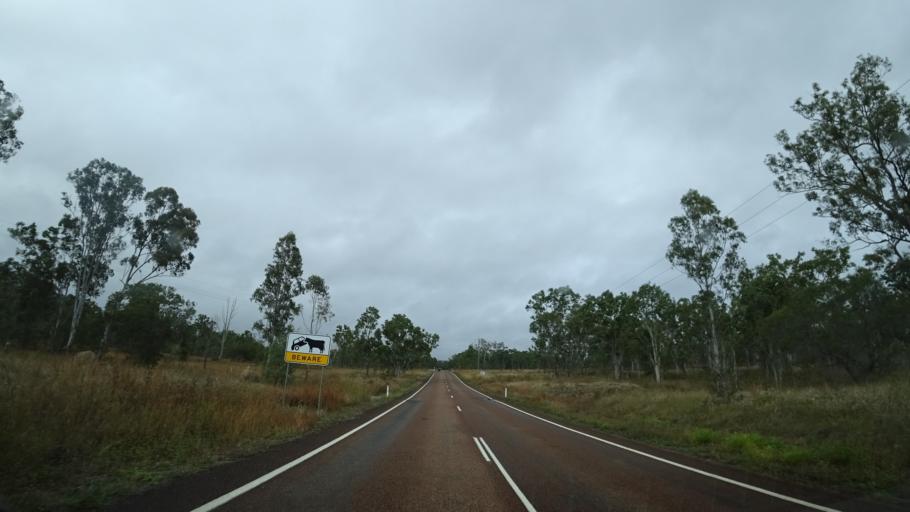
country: AU
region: Queensland
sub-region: Tablelands
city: Ravenshoe
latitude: -17.6713
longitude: 145.2377
